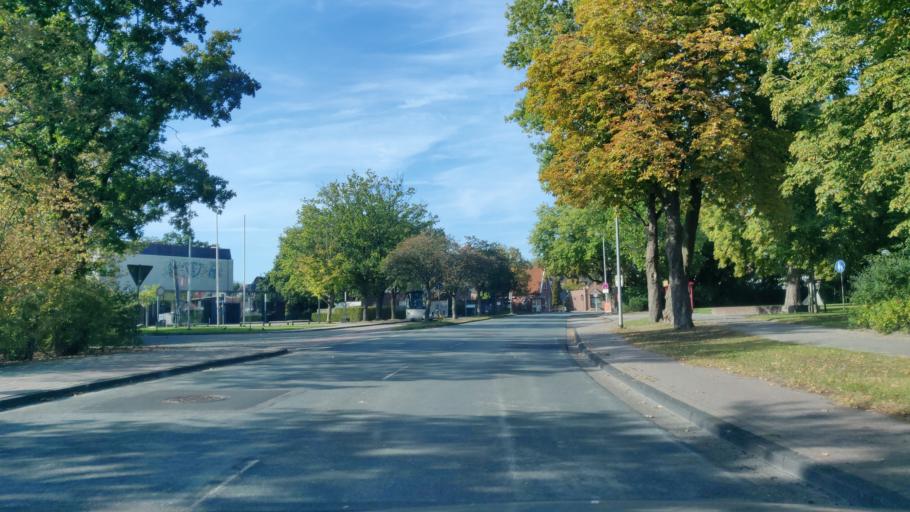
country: DE
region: Lower Saxony
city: Leer
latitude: 53.2267
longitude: 7.4428
